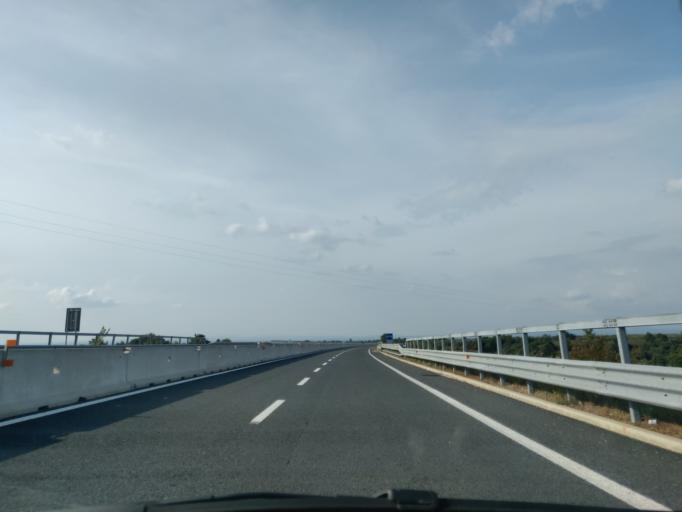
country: IT
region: Latium
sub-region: Provincia di Viterbo
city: Blera
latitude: 42.3290
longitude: 11.9858
